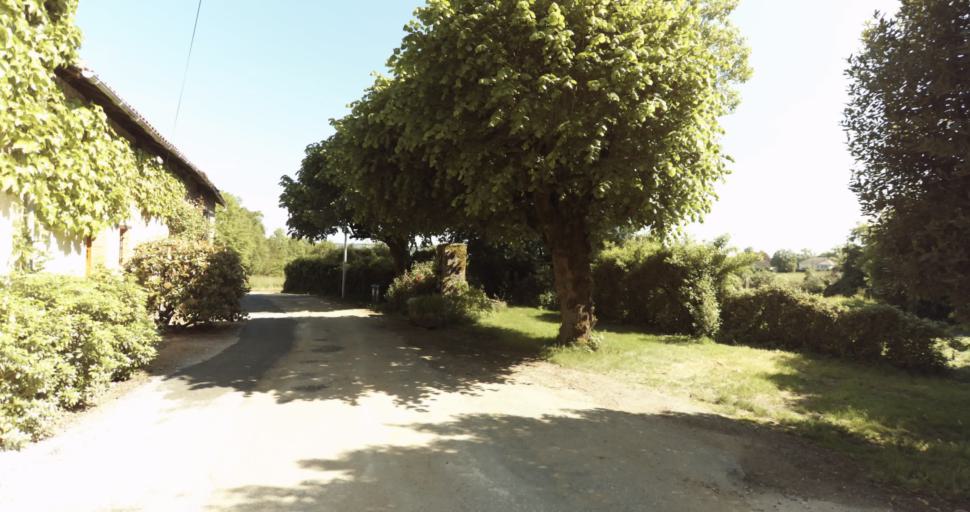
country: FR
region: Limousin
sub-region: Departement de la Haute-Vienne
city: Le Vigen
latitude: 45.7353
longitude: 1.2845
